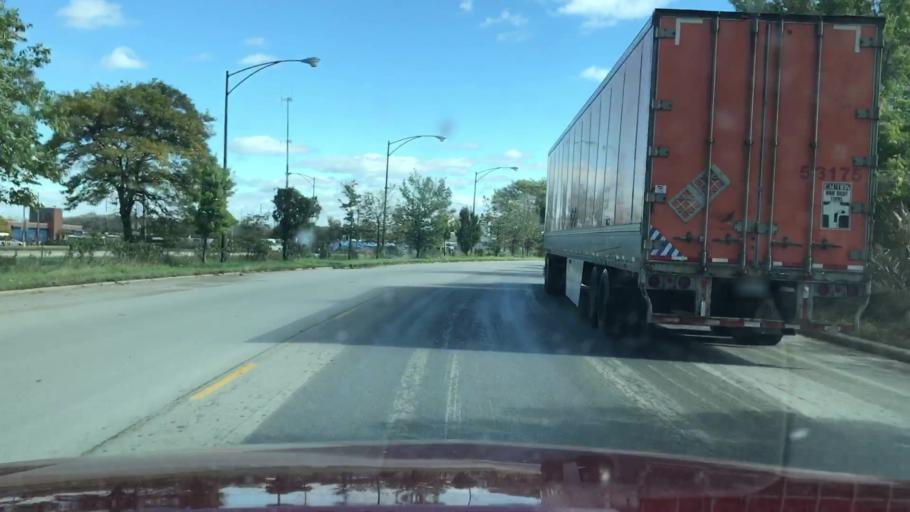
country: US
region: Illinois
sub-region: Cook County
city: Dolton
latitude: 41.7073
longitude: -87.5831
